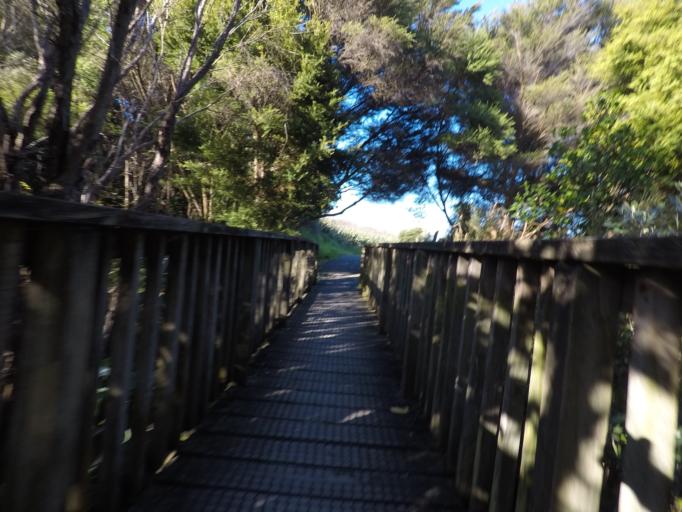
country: NZ
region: Auckland
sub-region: Auckland
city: Rosebank
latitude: -36.8420
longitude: 174.6581
